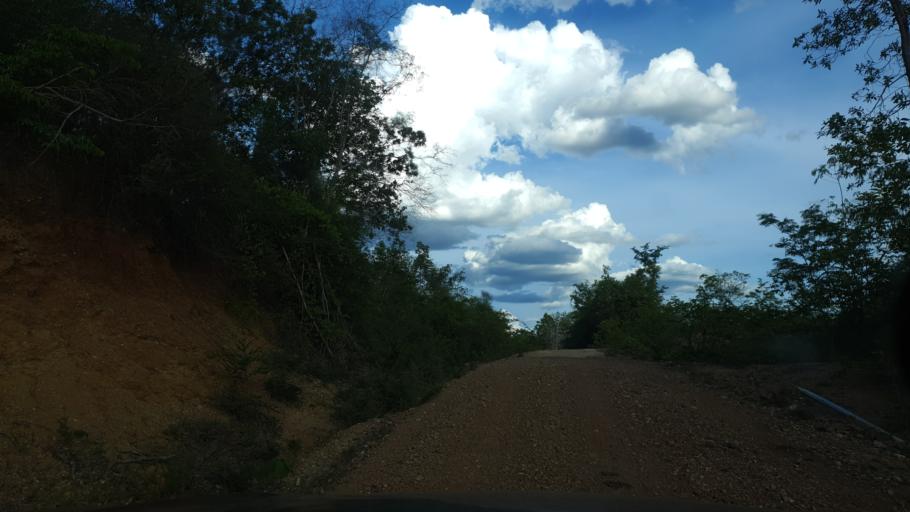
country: TH
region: Lampang
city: Sop Prap
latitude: 17.8874
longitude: 99.2898
